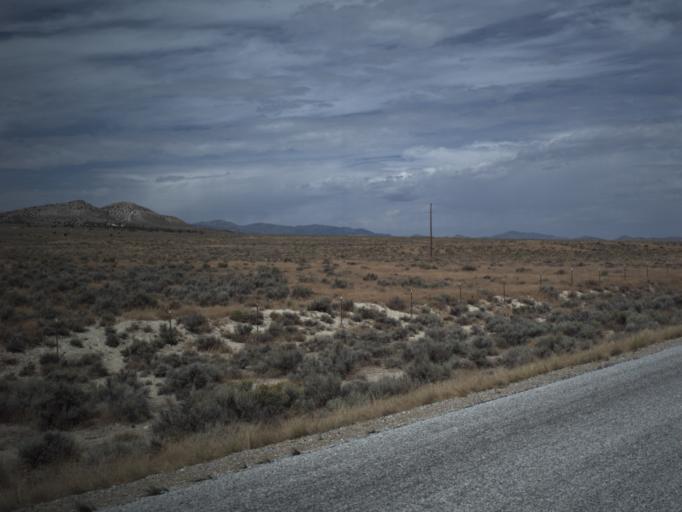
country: US
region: Utah
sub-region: Tooele County
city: Wendover
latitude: 41.5086
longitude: -113.6016
